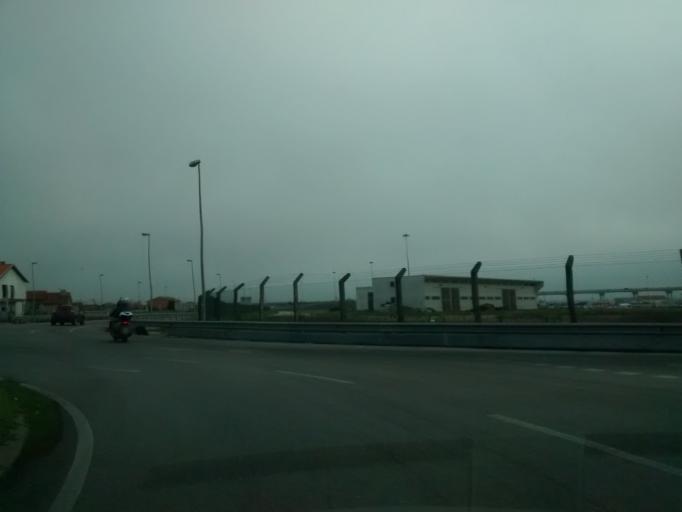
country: PT
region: Aveiro
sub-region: Ilhavo
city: Gafanha da Encarnacao
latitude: 40.6332
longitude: -8.7295
